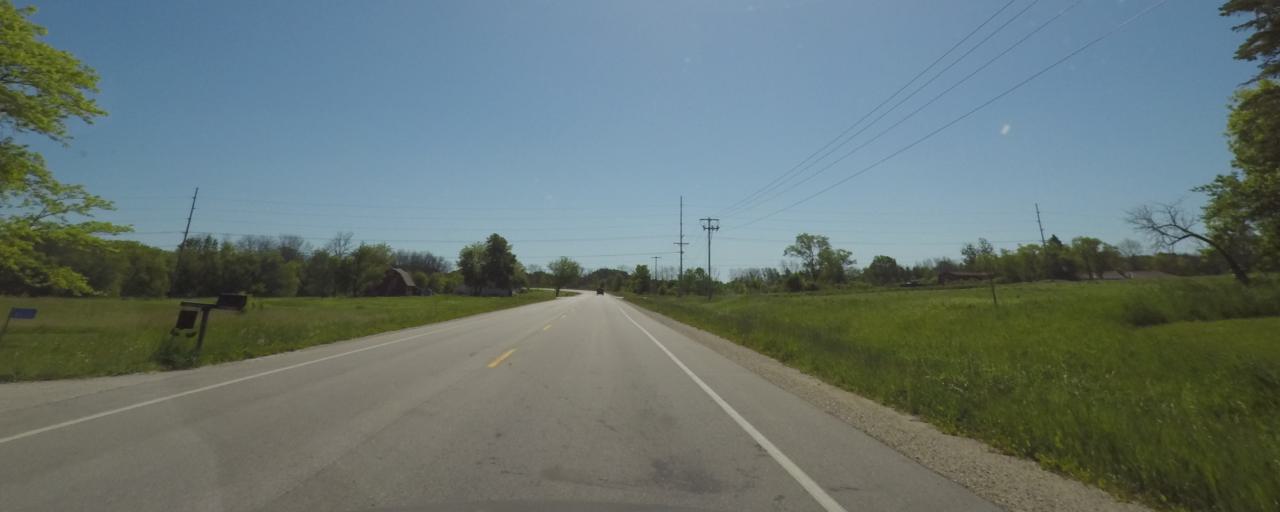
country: US
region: Wisconsin
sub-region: Sheboygan County
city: Plymouth
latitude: 43.7462
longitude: -87.9231
